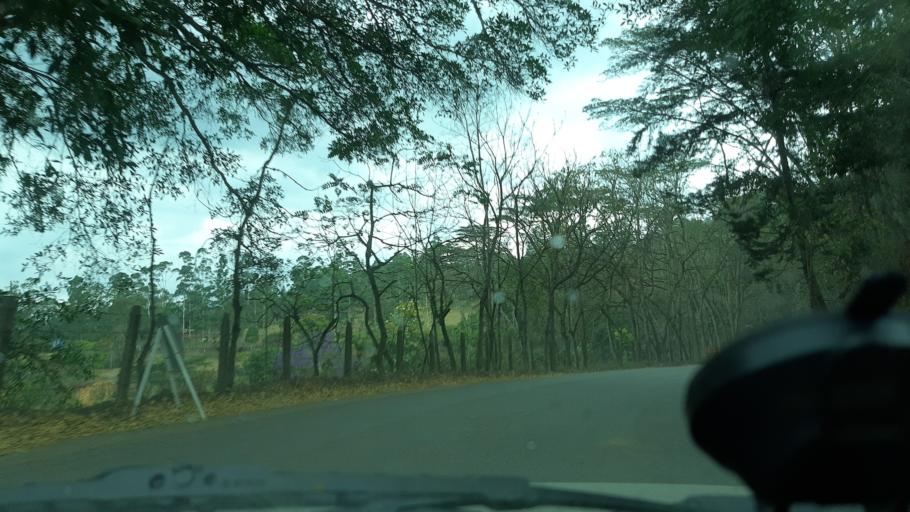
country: CO
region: Boyaca
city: Garagoa
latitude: 5.0714
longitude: -73.3798
